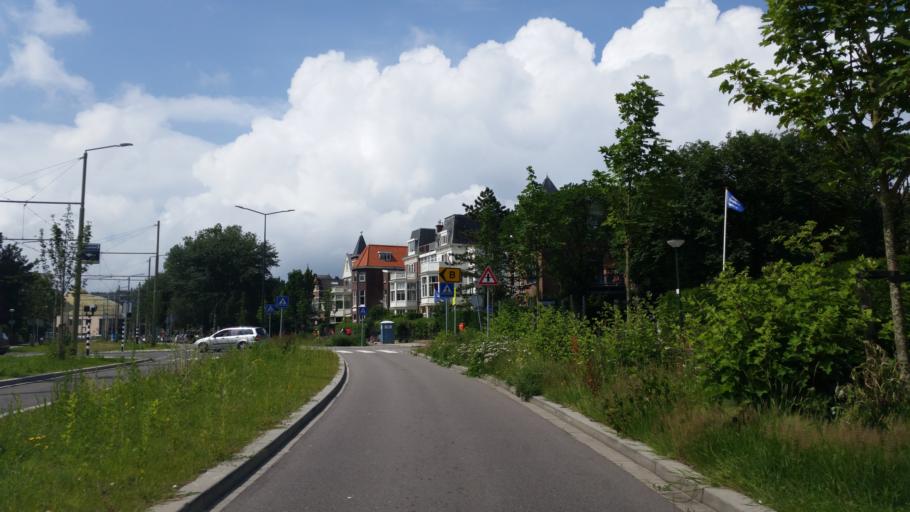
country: NL
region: South Holland
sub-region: Gemeente Den Haag
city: Scheveningen
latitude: 52.1092
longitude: 4.2872
